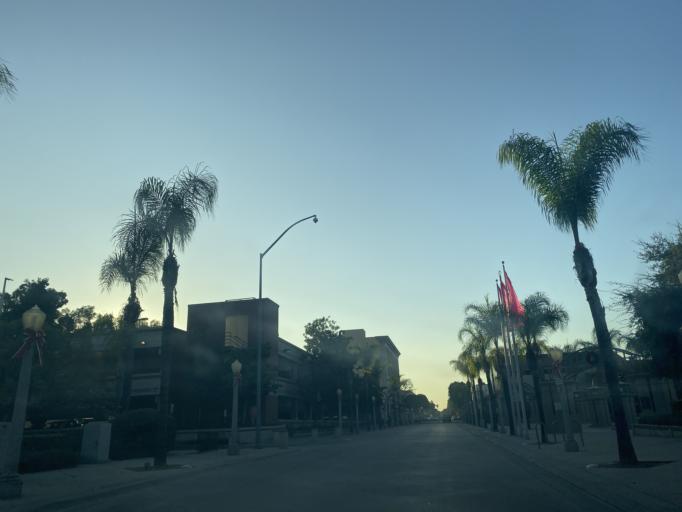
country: US
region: California
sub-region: Orange County
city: Fullerton
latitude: 33.8724
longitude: -117.9223
